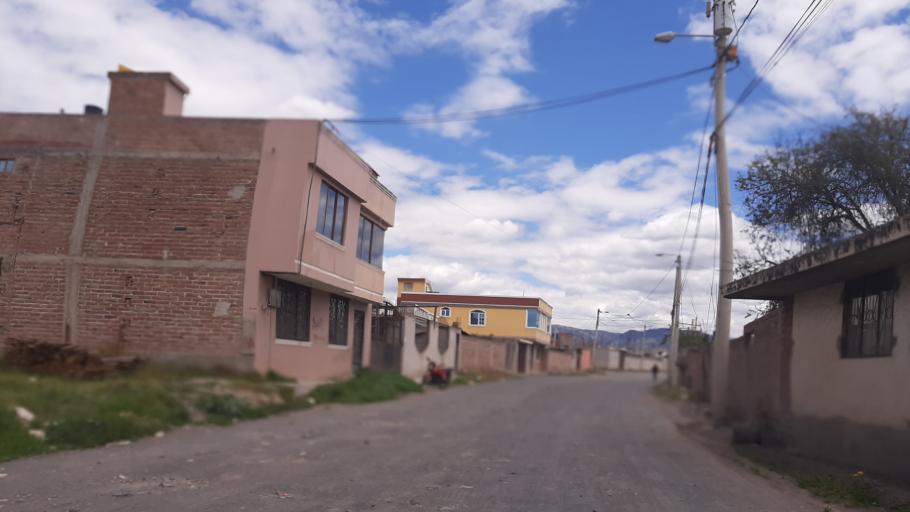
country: EC
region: Chimborazo
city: Riobamba
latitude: -1.6557
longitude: -78.6361
